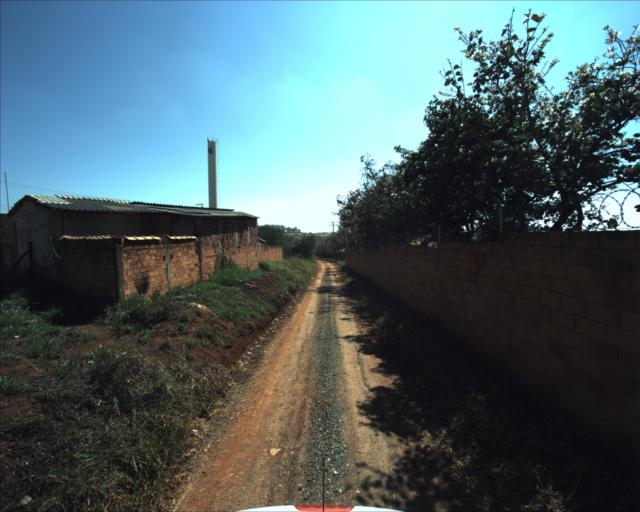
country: BR
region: Sao Paulo
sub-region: Sorocaba
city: Sorocaba
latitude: -23.4406
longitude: -47.5355
